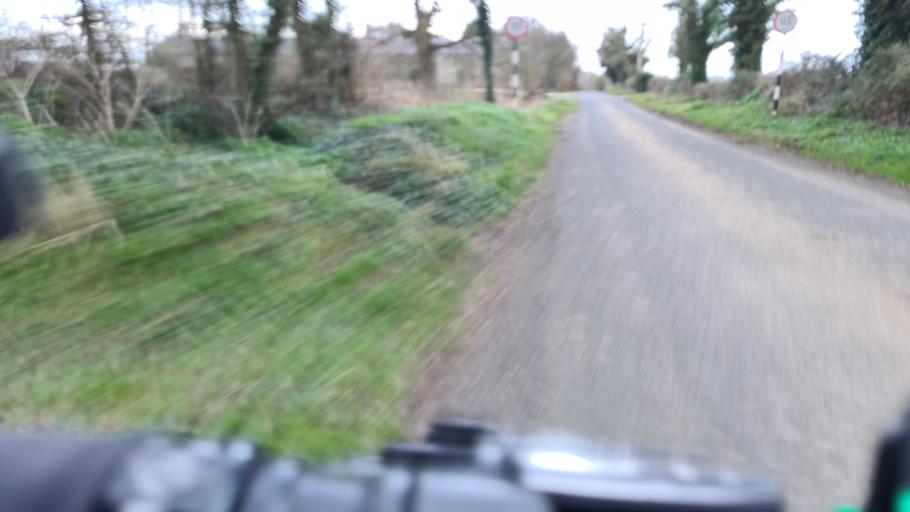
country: IE
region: Leinster
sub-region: Kildare
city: Maynooth
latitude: 53.3402
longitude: -6.6013
